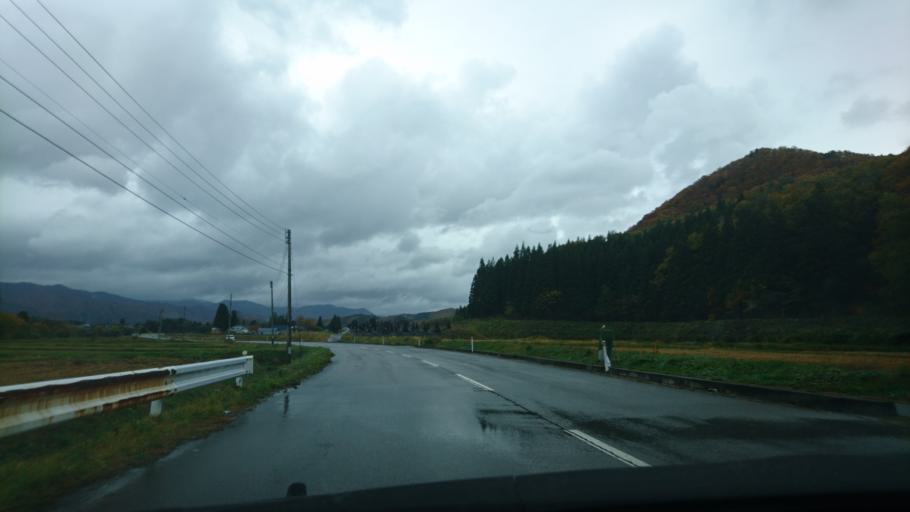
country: JP
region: Akita
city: Yokotemachi
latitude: 39.3821
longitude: 140.7664
